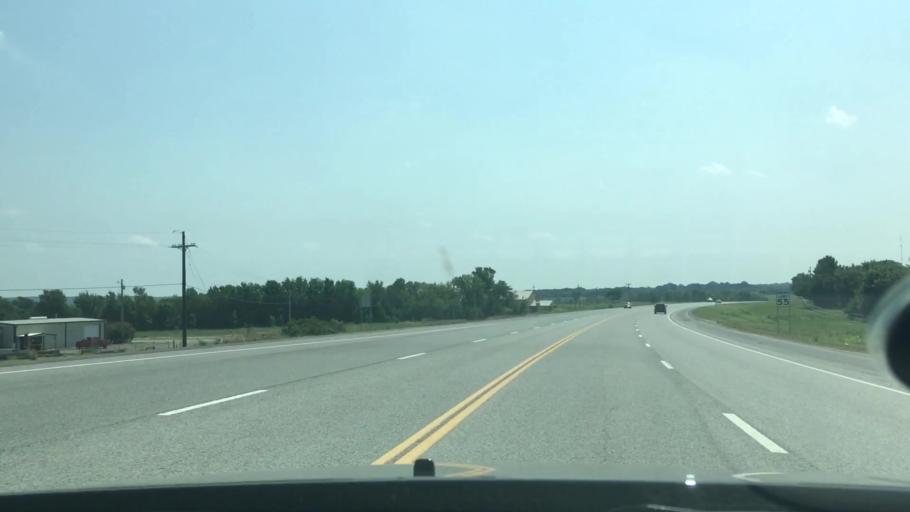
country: US
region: Oklahoma
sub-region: Atoka County
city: Atoka
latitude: 34.3722
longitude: -96.1089
